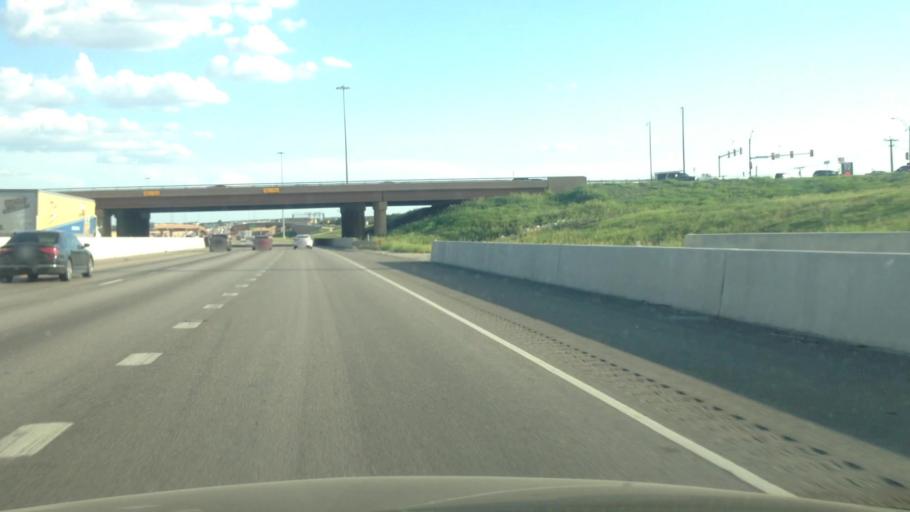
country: US
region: Texas
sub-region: Tarrant County
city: Blue Mound
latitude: 32.8743
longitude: -97.3173
